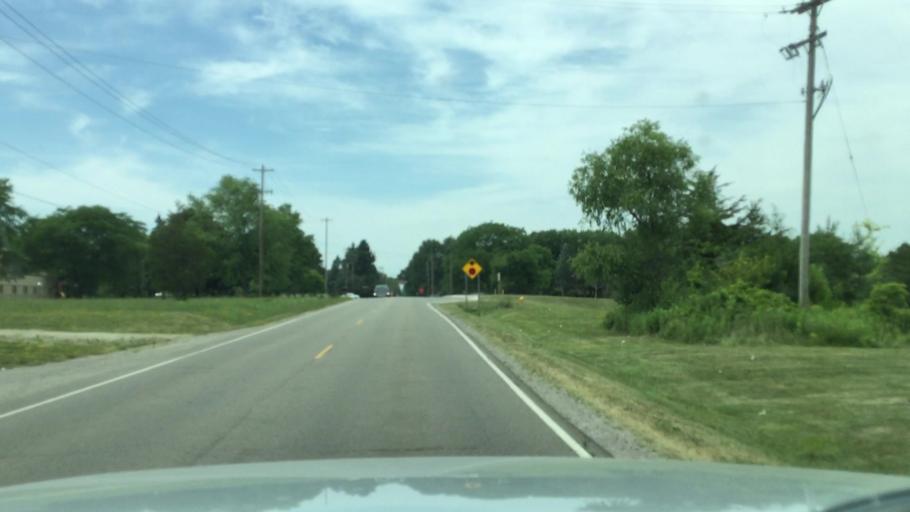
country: US
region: Michigan
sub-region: Genesee County
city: Swartz Creek
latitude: 43.0166
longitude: -83.7795
